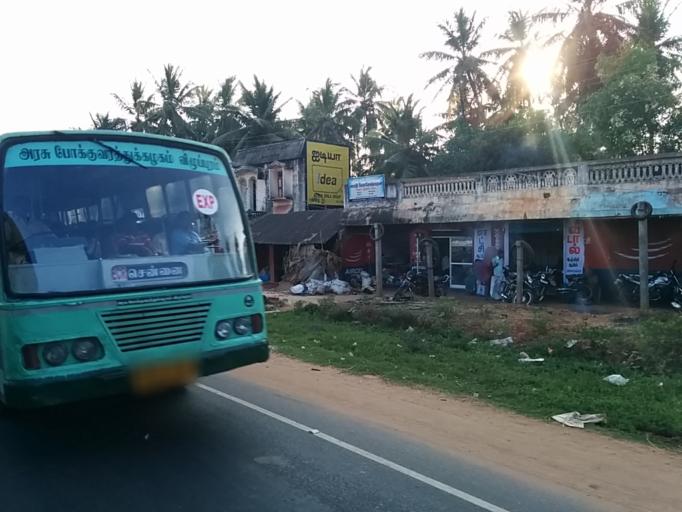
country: IN
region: Tamil Nadu
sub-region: Villupuram
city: Auroville
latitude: 12.0064
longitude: 79.8553
